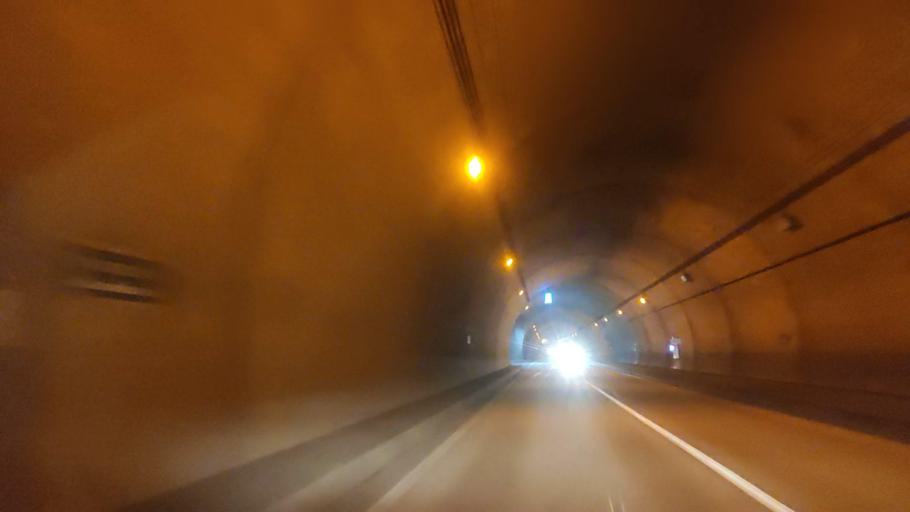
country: JP
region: Hokkaido
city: Date
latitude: 42.5585
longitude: 140.7577
